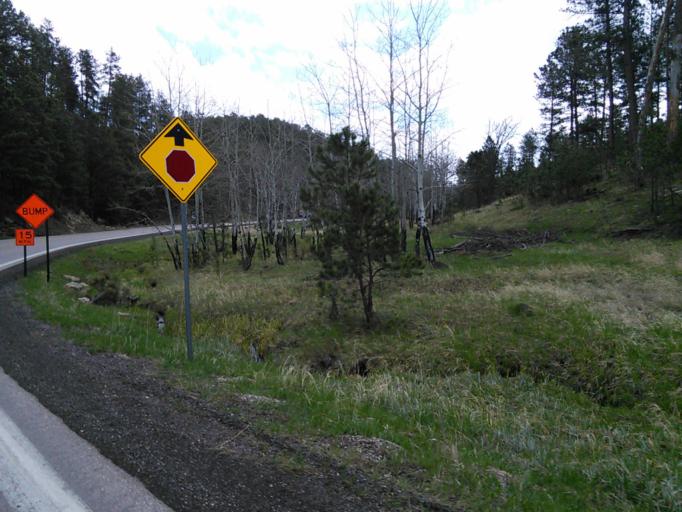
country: US
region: South Dakota
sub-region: Custer County
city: Custer
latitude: 43.7598
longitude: -103.4823
